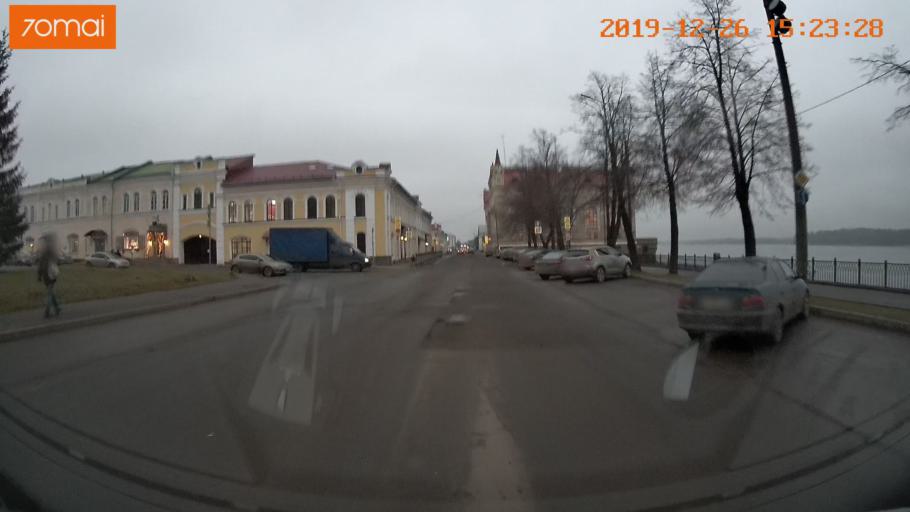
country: RU
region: Jaroslavl
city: Rybinsk
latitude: 58.0489
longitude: 38.8583
